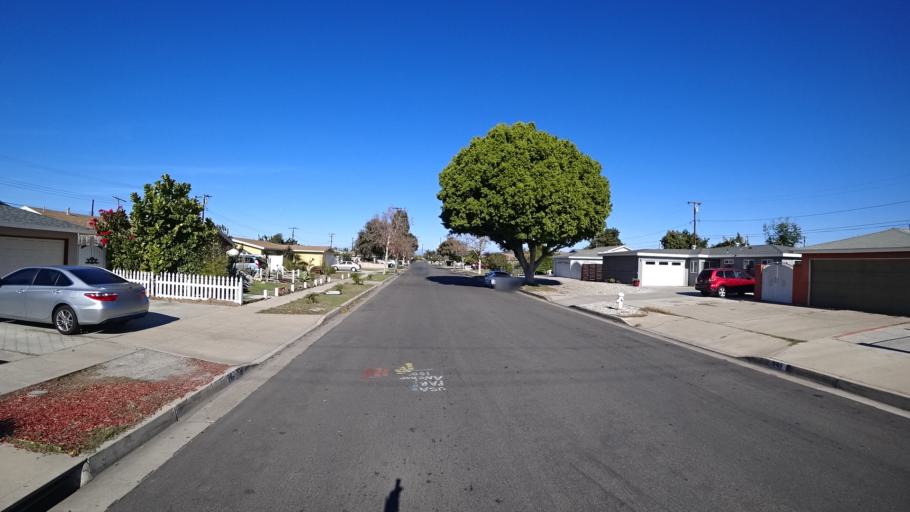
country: US
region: California
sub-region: Orange County
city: Garden Grove
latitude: 33.7527
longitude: -117.9350
